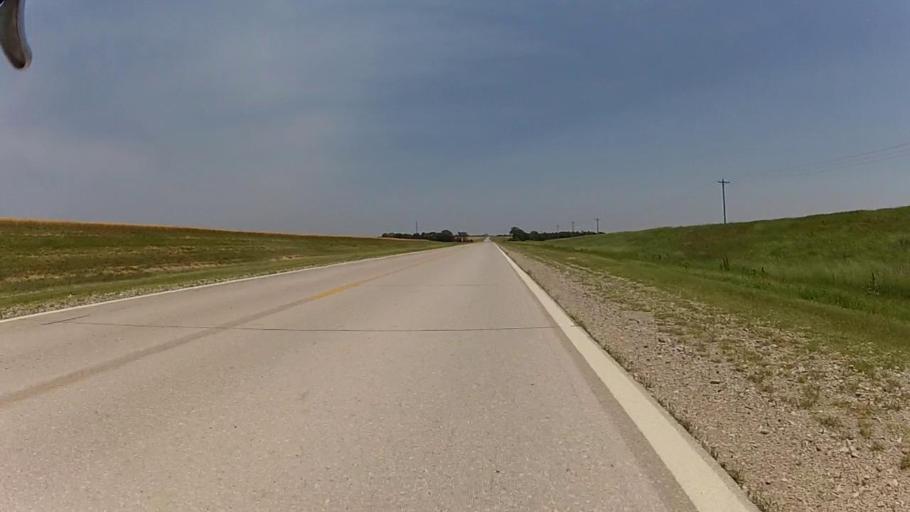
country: US
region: Kansas
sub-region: Sumner County
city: Wellington
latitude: 37.0573
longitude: -97.2946
